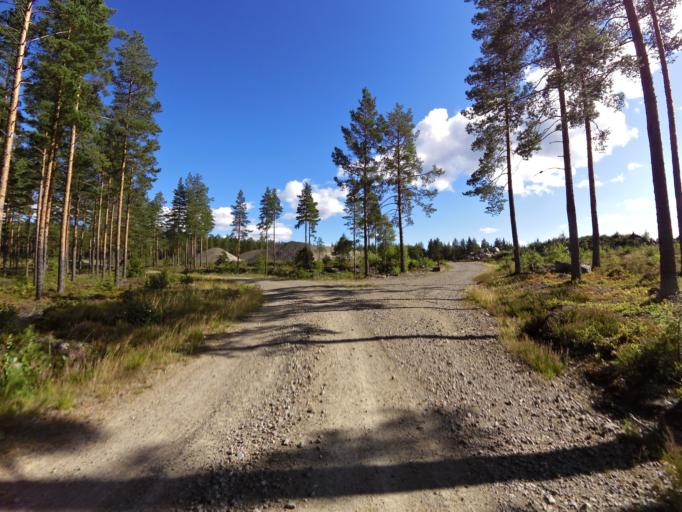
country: SE
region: Gaevleborg
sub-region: Ockelbo Kommun
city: Ockelbo
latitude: 60.8259
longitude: 16.7602
